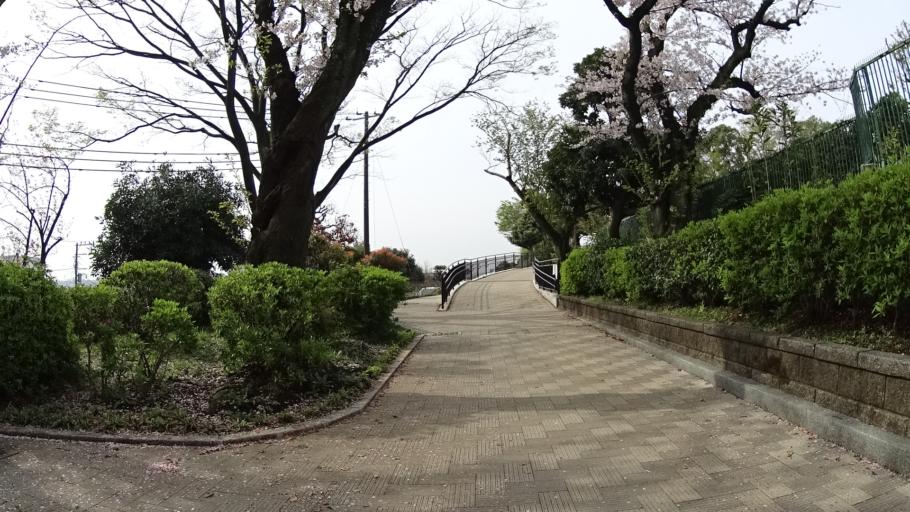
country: JP
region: Kanagawa
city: Yokohama
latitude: 35.4458
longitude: 139.6236
